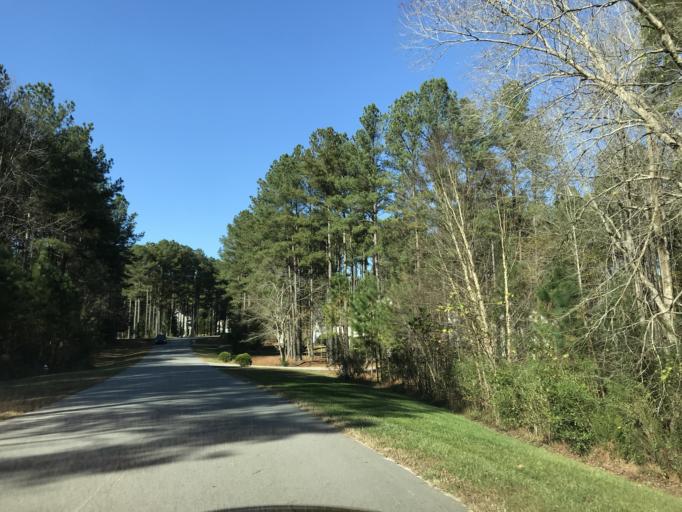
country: US
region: North Carolina
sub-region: Wake County
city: Rolesville
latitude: 35.9643
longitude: -78.3681
